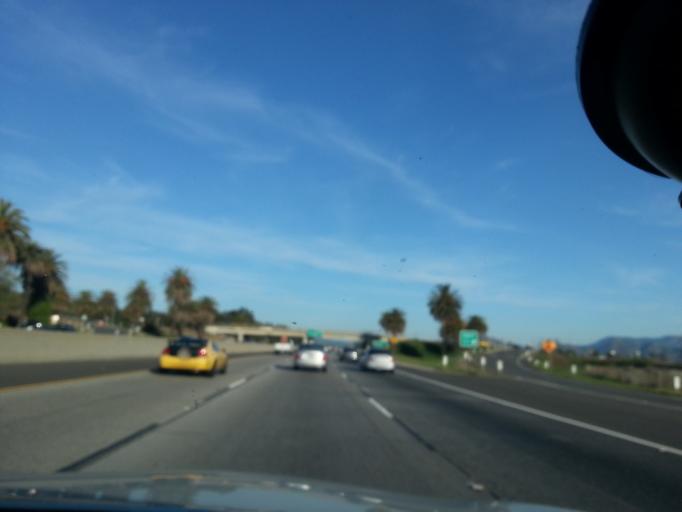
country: US
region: California
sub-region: Ventura County
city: El Rio
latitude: 34.2218
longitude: -119.1042
